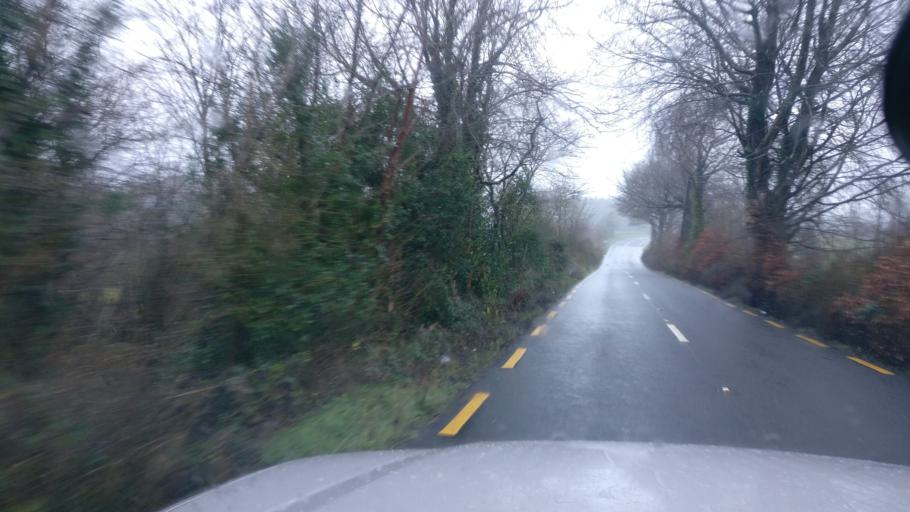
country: IE
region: Connaught
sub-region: County Galway
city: Loughrea
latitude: 53.1374
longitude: -8.4657
